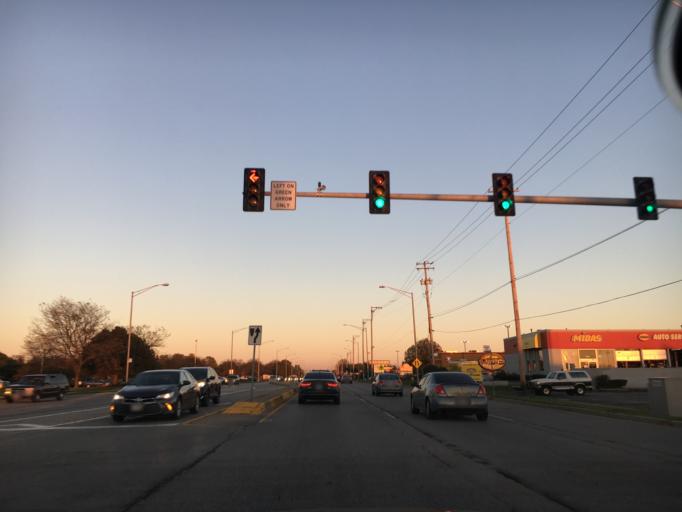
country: US
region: Illinois
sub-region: Cook County
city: Tinley Park
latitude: 41.6023
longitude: -87.7913
